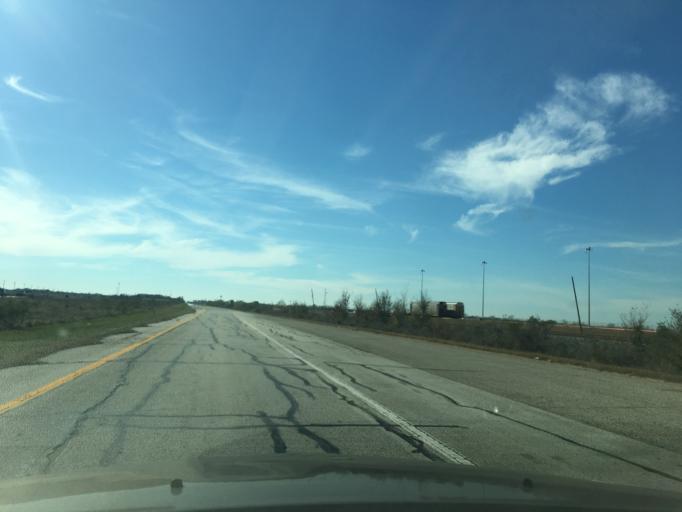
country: US
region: Texas
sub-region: Wharton County
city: East Bernard
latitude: 29.4611
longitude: -95.9778
